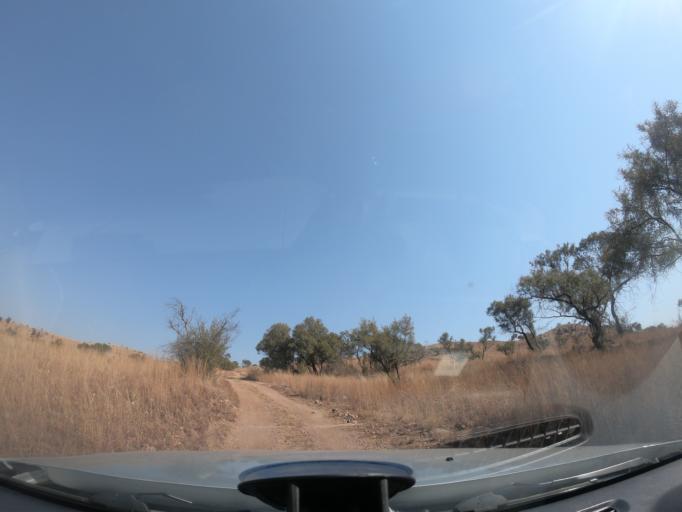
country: ZA
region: Gauteng
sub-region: City of Johannesburg Metropolitan Municipality
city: Diepsloot
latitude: -25.8290
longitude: 28.0266
